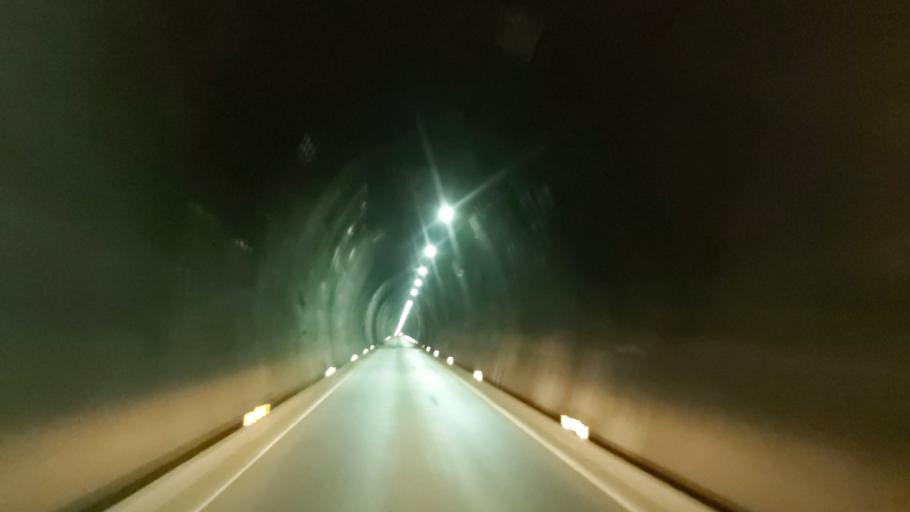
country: CL
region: Araucania
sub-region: Provincia de Cautin
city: Vilcun
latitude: -38.5452
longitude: -71.5041
